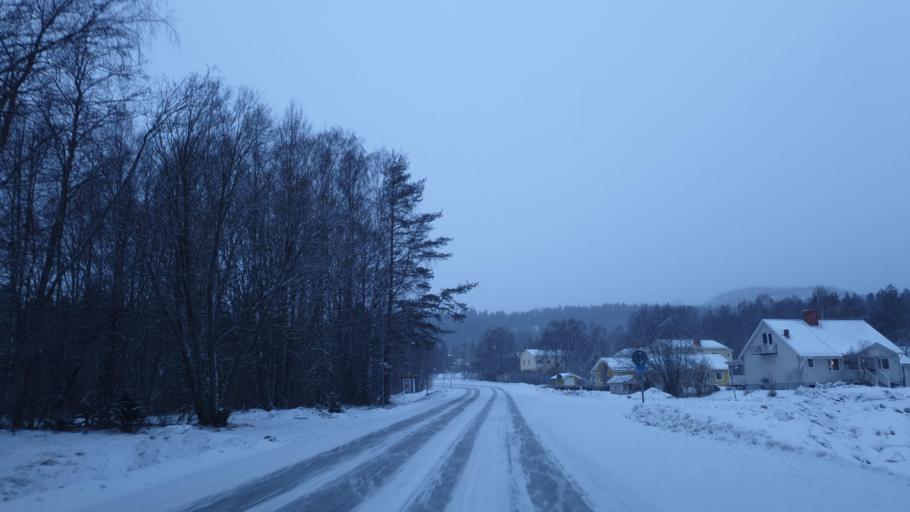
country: SE
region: Vaesternorrland
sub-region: OErnskoeldsviks Kommun
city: Ornskoldsvik
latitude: 63.3002
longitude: 18.6392
